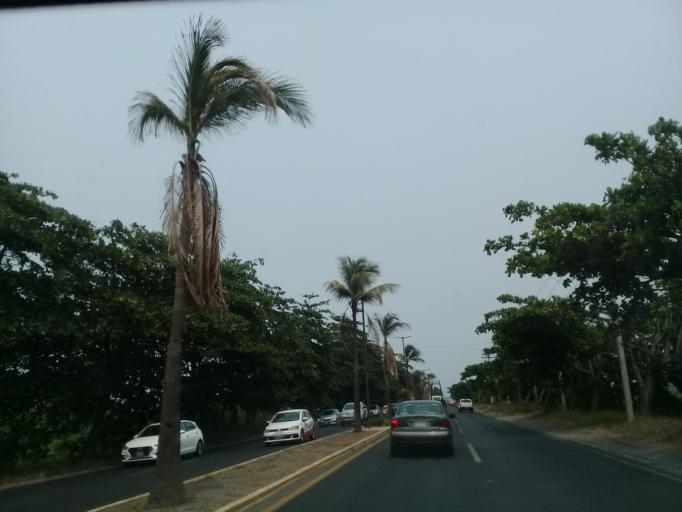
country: MX
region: Veracruz
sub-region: Veracruz
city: Hacienda Sotavento
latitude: 19.1464
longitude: -96.1657
